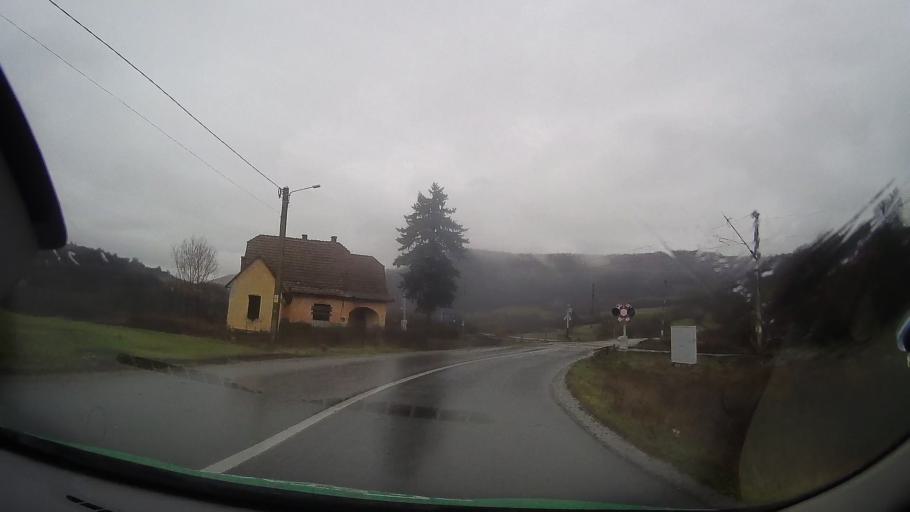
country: RO
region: Bistrita-Nasaud
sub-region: Comuna Mariselu
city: Mariselu
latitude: 47.0148
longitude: 24.5444
